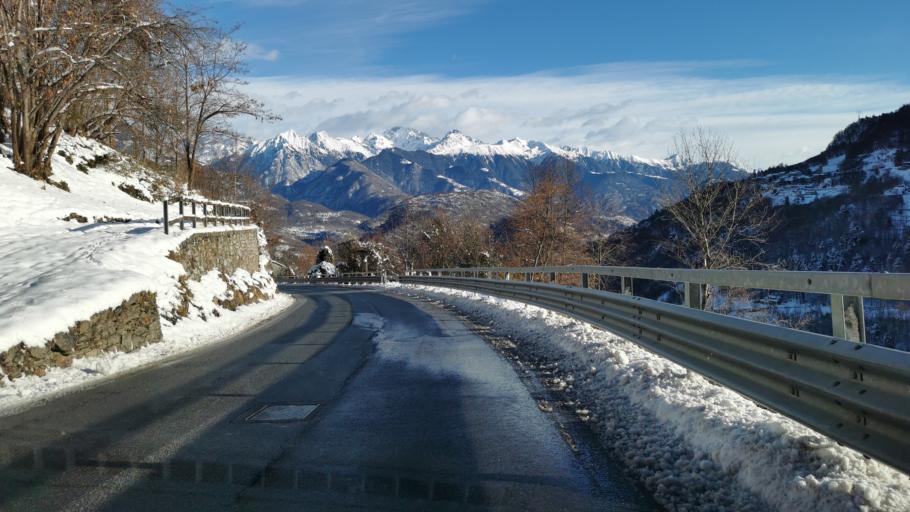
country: IT
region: Lombardy
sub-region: Provincia di Sondrio
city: Bema
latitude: 46.1177
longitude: 9.5599
